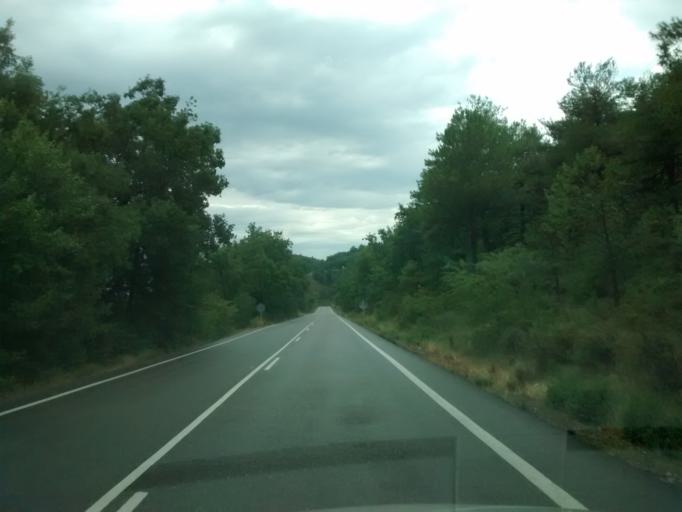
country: ES
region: Aragon
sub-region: Provincia de Huesca
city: Labuerda
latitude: 42.4398
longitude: 0.1304
